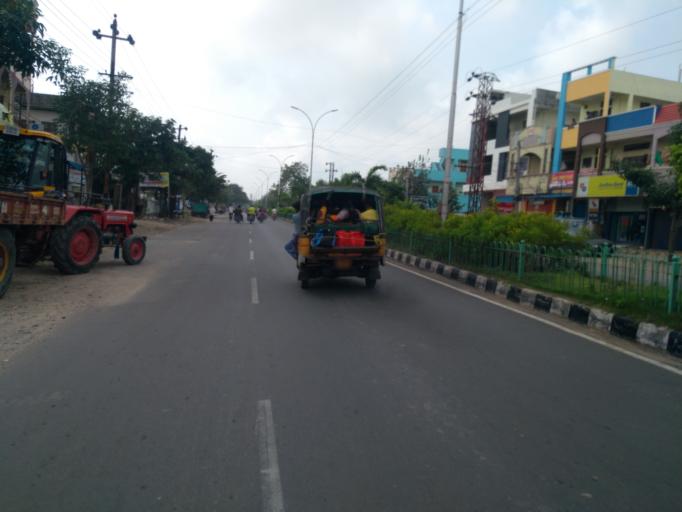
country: IN
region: Telangana
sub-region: Warangal
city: Warangal
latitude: 17.9549
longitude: 79.6007
